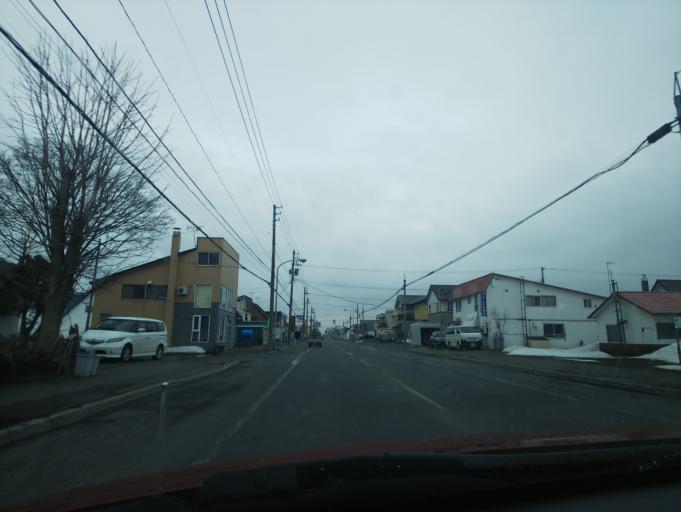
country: JP
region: Hokkaido
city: Nayoro
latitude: 44.3536
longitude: 142.4503
